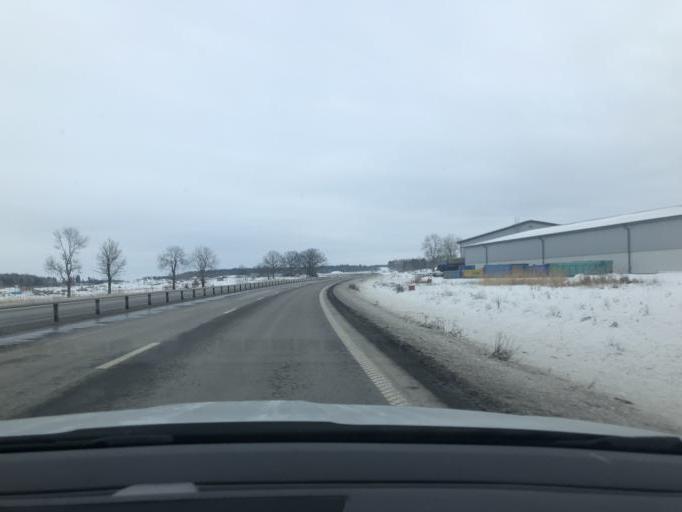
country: SE
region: OEstergoetland
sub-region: Linkopings Kommun
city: Sturefors
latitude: 58.3999
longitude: 15.6987
